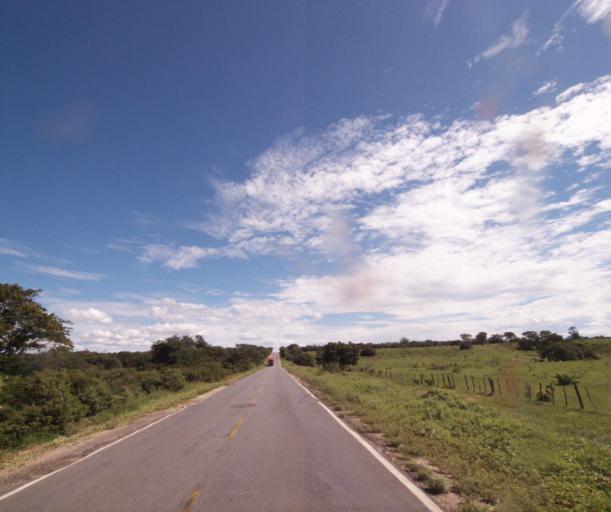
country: BR
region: Bahia
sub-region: Guanambi
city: Guanambi
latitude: -14.5648
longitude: -42.7027
